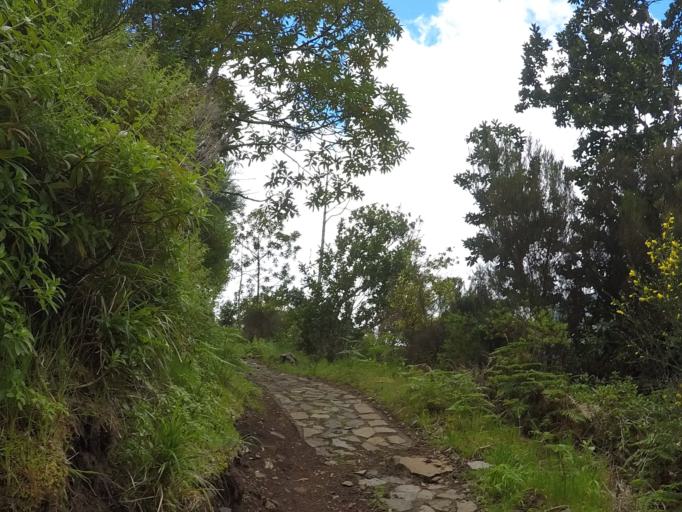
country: PT
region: Madeira
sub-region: Camara de Lobos
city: Curral das Freiras
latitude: 32.7422
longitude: -17.0056
